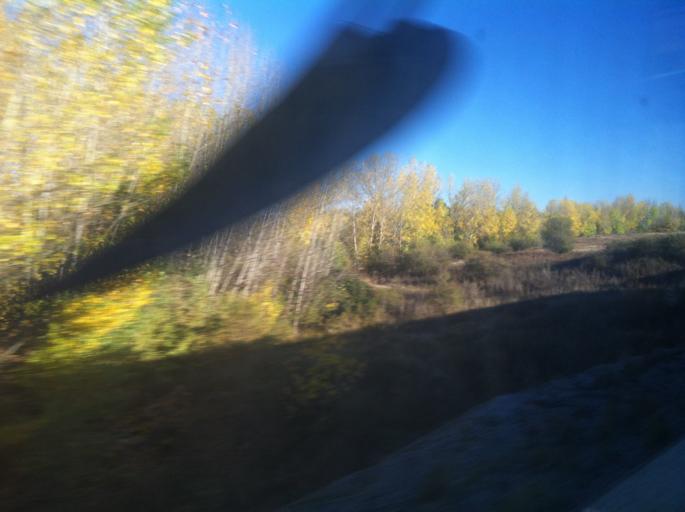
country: ES
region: Castille and Leon
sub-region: Provincia de Valladolid
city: Cubillas de Santa Marta
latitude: 41.7993
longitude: -4.5888
